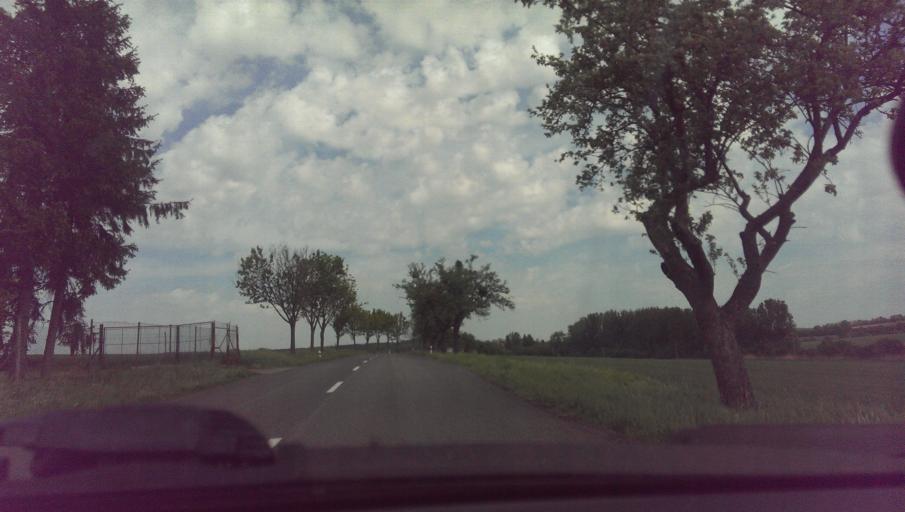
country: CZ
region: Zlin
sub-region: Okres Zlin
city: Otrokovice
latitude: 49.2255
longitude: 17.5361
